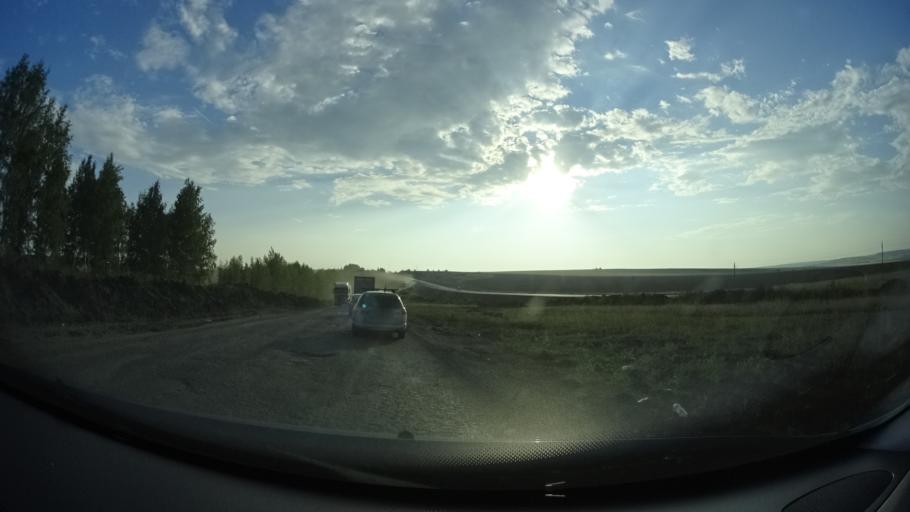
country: RU
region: Samara
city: Kamyshla
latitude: 54.0683
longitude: 52.1716
